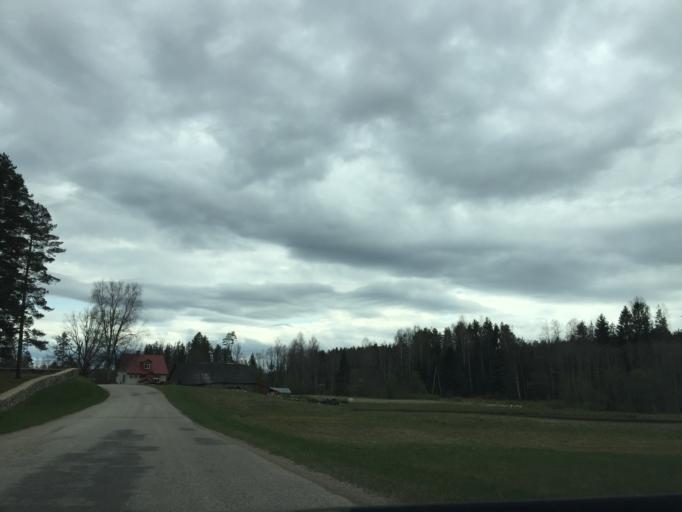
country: LV
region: Jaunpiebalga
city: Jaunpiebalga
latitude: 57.1727
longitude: 26.0628
